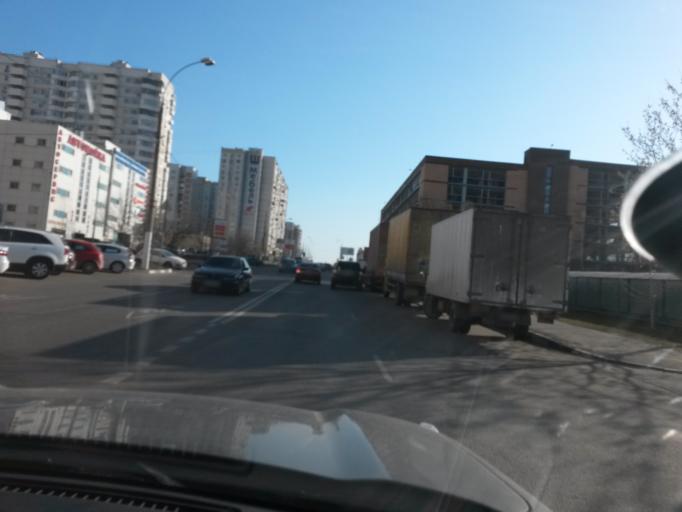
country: RU
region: Moscow
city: Chertanovo Yuzhnoye
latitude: 55.5712
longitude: 37.5640
